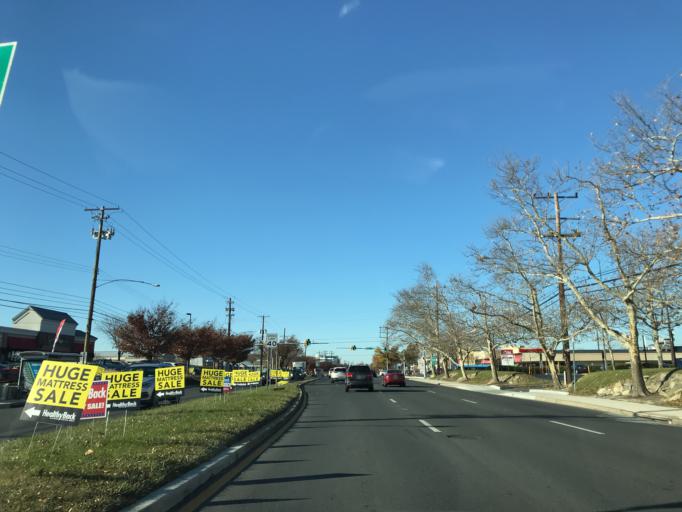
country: US
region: Maryland
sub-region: Montgomery County
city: North Bethesda
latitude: 39.0610
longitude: -77.1232
